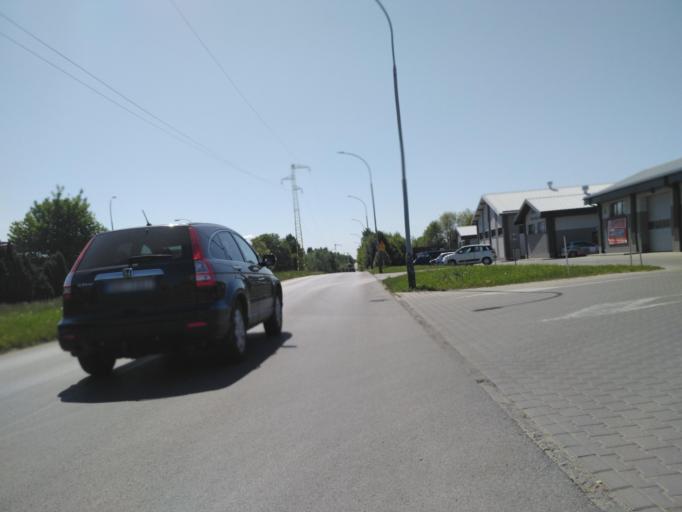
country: PL
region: Subcarpathian Voivodeship
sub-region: Krosno
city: Krosno
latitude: 49.6793
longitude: 21.7816
